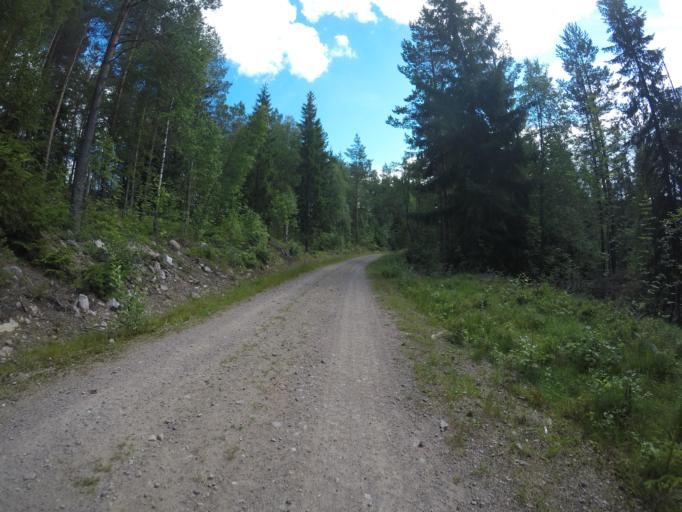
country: SE
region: Vaermland
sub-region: Filipstads Kommun
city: Lesjofors
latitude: 60.0695
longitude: 14.4595
